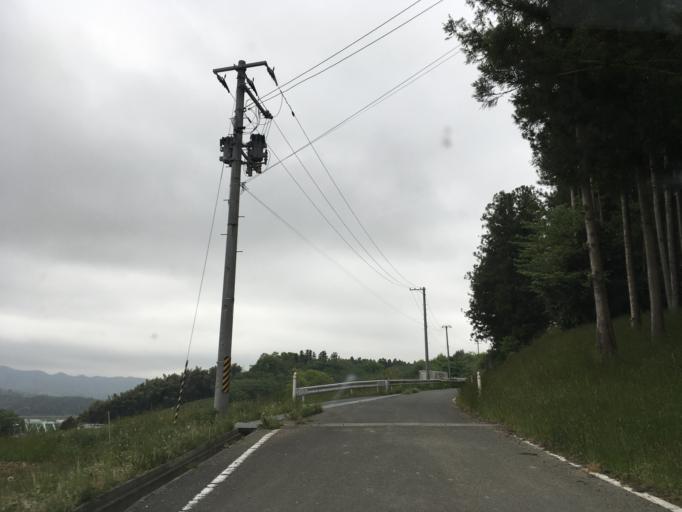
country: JP
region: Miyagi
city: Wakuya
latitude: 38.7087
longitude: 141.2830
